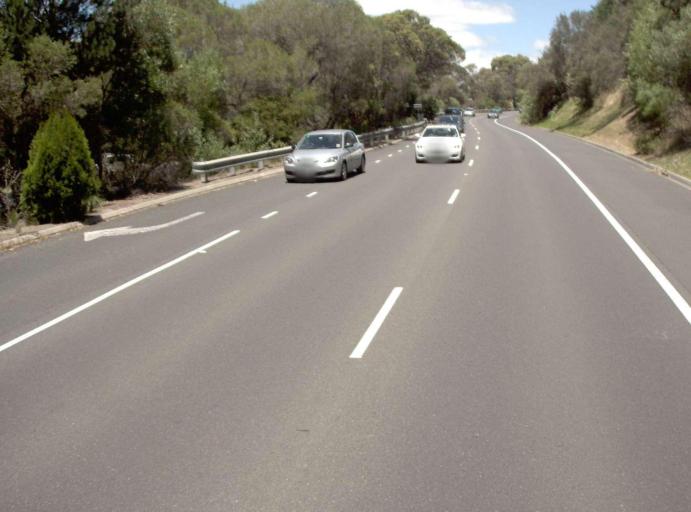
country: AU
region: Victoria
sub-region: Mornington Peninsula
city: Mount Eliza
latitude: -38.1823
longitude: 145.0961
